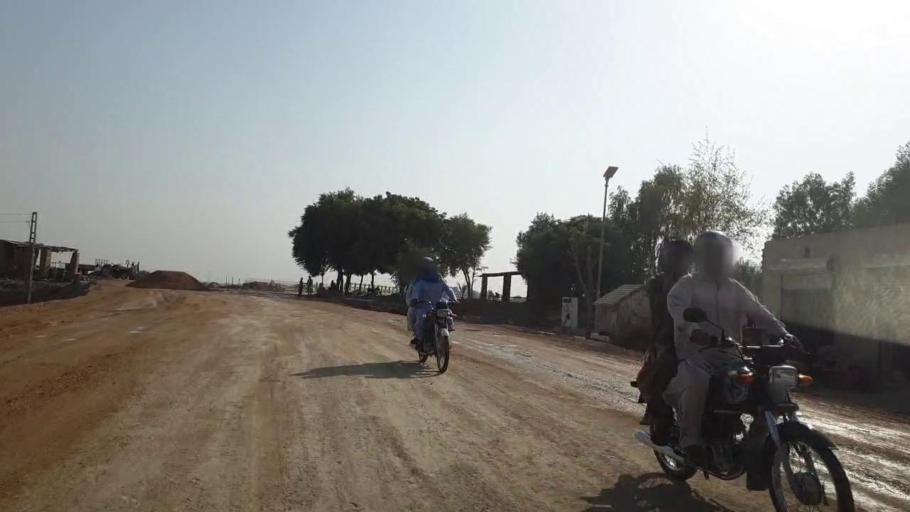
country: PK
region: Sindh
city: Bhan
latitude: 26.5019
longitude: 67.7822
